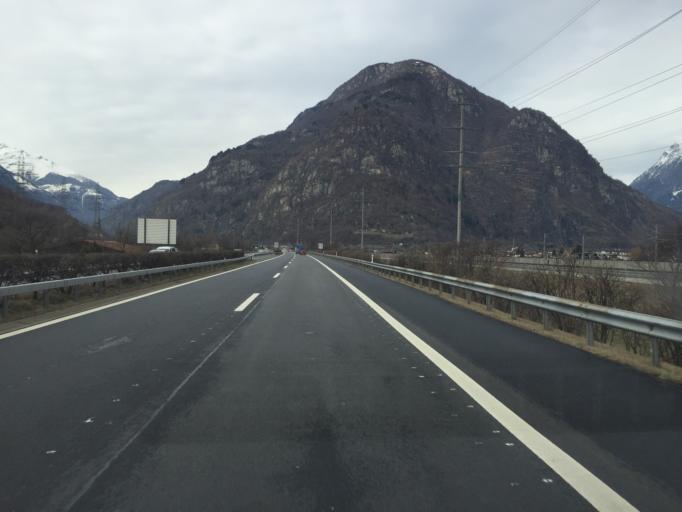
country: CH
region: Ticino
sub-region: Riviera District
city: Biasca
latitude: 46.3483
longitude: 8.9644
